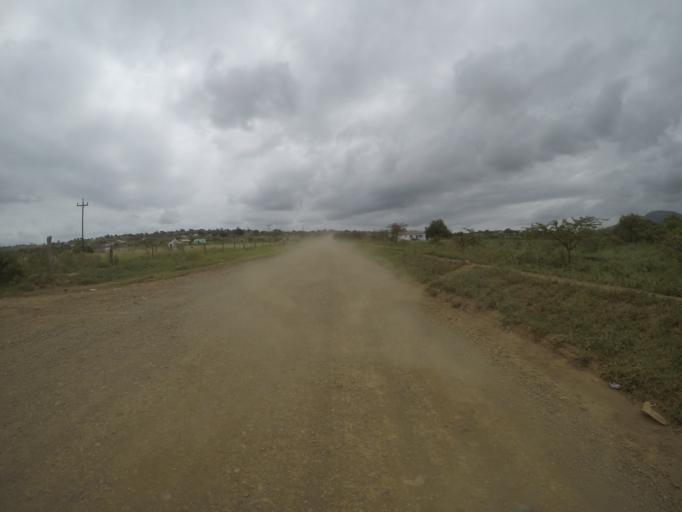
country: ZA
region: KwaZulu-Natal
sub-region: uThungulu District Municipality
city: Empangeni
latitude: -28.5867
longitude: 31.8451
